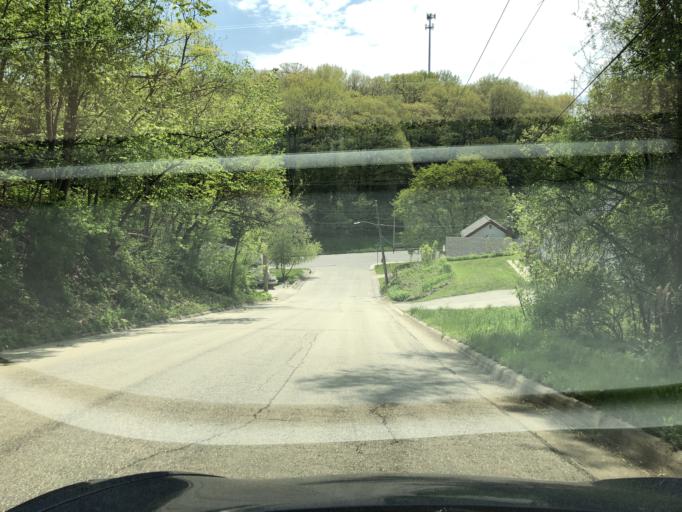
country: US
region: Iowa
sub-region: Dubuque County
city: Dubuque
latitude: 42.4825
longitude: -90.6693
